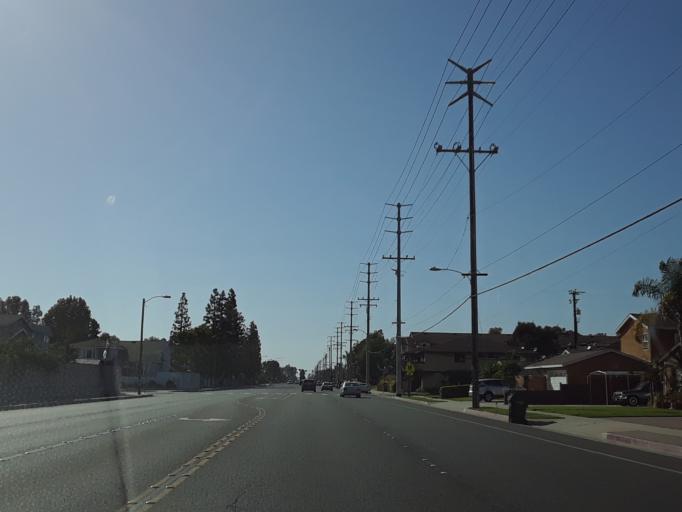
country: US
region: California
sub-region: Orange County
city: Huntington Beach
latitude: 33.6867
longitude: -117.9845
